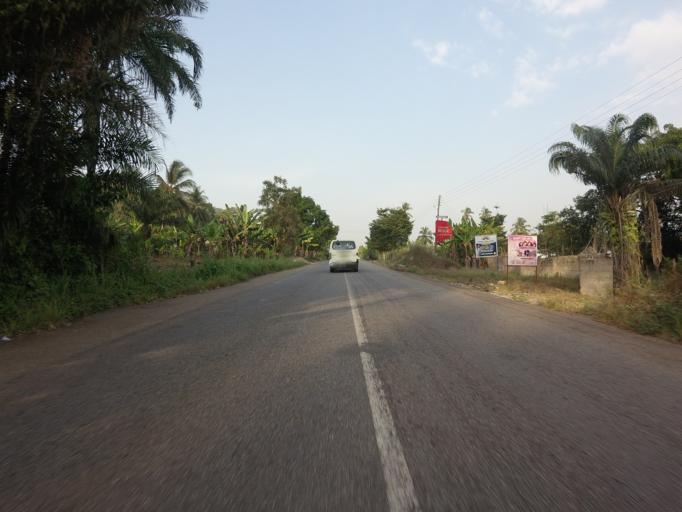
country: GH
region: Volta
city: Ho
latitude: 6.5342
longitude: 0.2822
